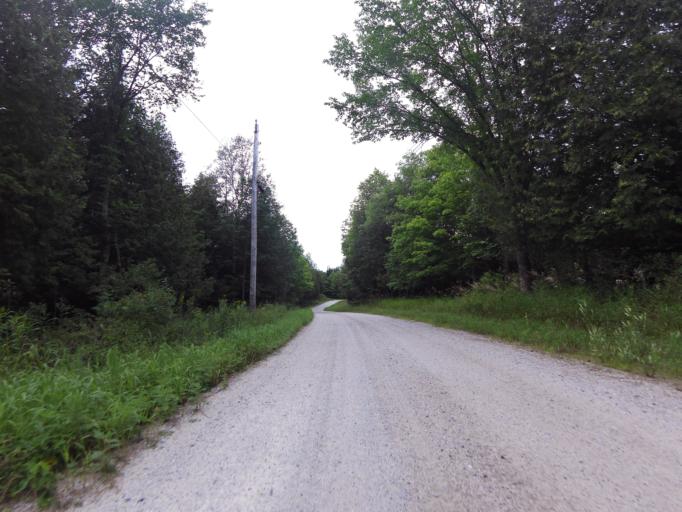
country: CA
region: Ontario
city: Perth
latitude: 44.8406
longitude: -76.5915
